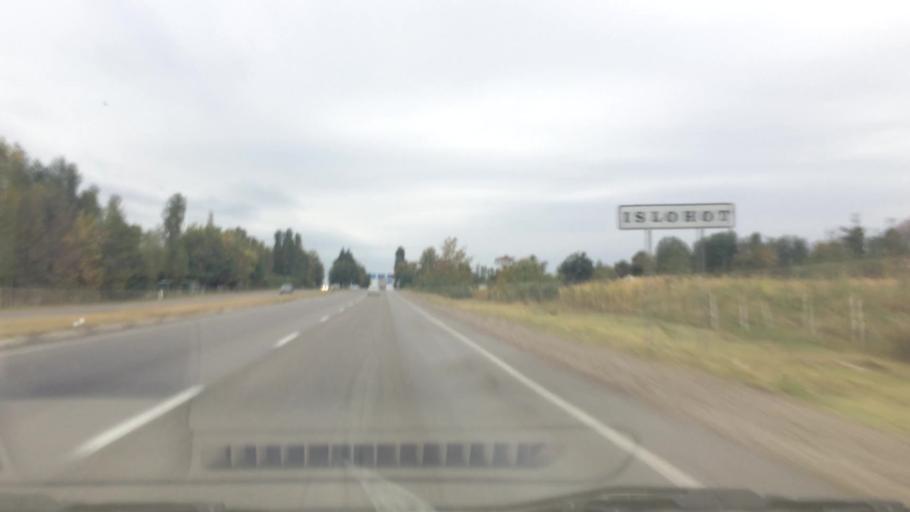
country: UZ
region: Toshkent
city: Amir Timur
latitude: 41.0886
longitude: 68.9495
